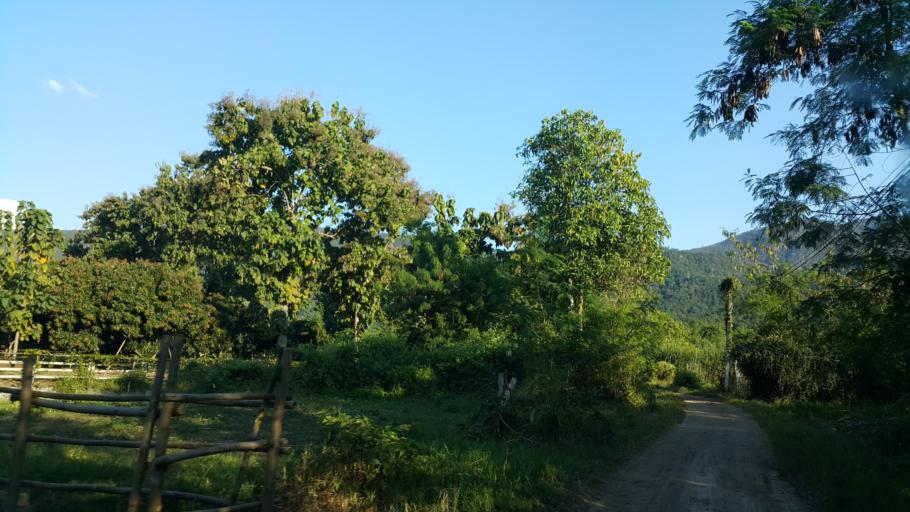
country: TH
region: Chiang Mai
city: Mae On
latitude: 18.7533
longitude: 99.2601
